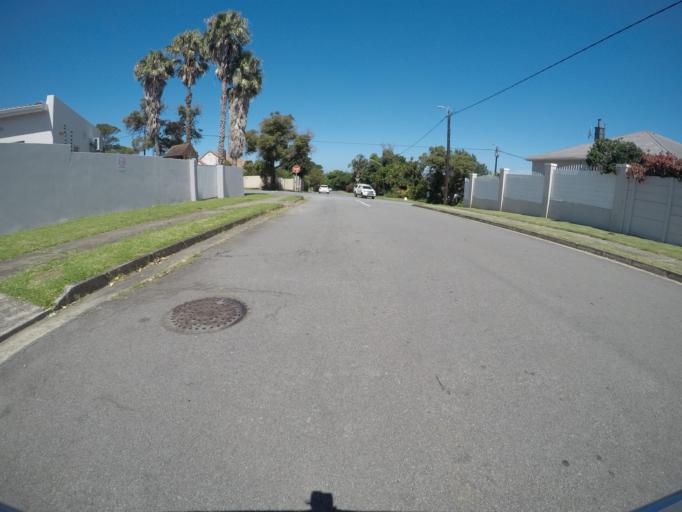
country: ZA
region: Eastern Cape
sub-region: Buffalo City Metropolitan Municipality
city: East London
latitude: -32.9797
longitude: 27.9229
